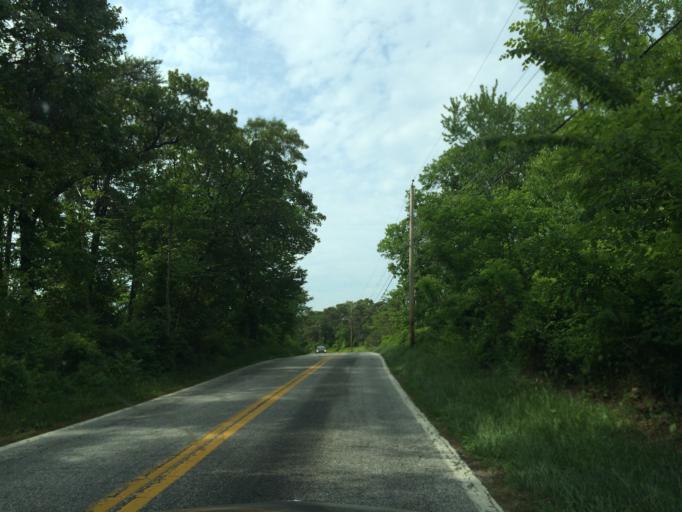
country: US
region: Maryland
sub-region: Baltimore County
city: Reisterstown
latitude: 39.4221
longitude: -76.8404
